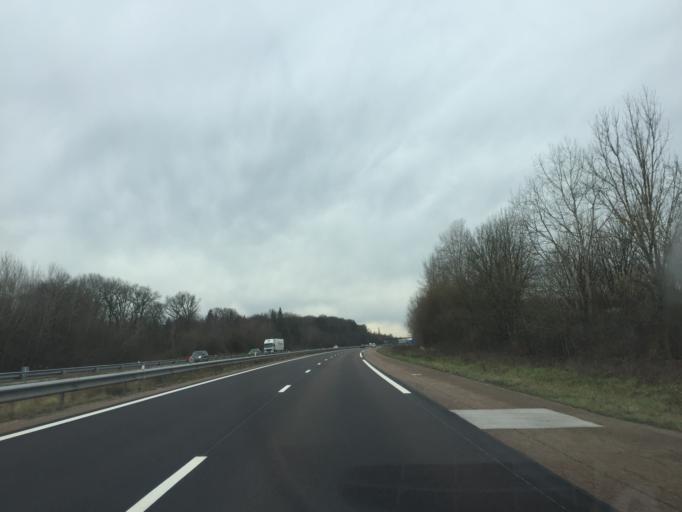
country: FR
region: Franche-Comte
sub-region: Departement du Jura
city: Mont-sous-Vaudrey
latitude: 46.8481
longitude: 5.5678
